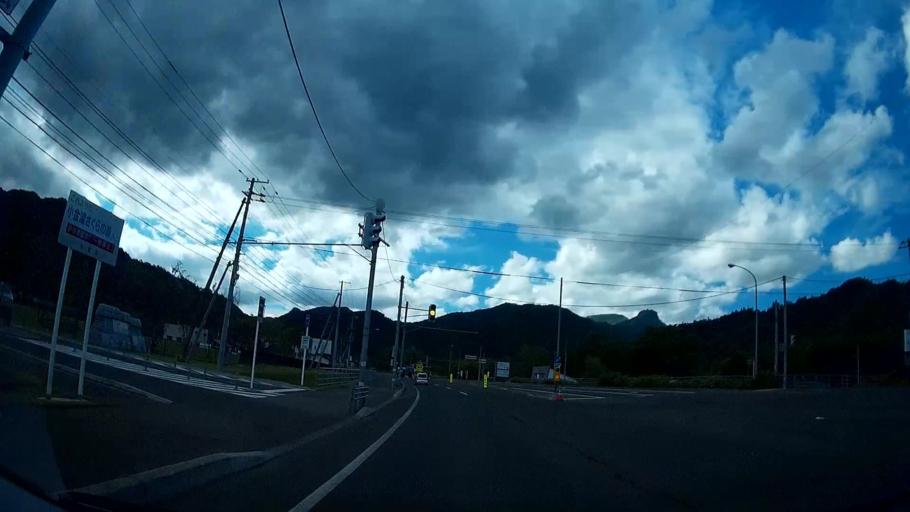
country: JP
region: Hokkaido
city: Sapporo
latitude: 42.9653
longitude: 141.2201
